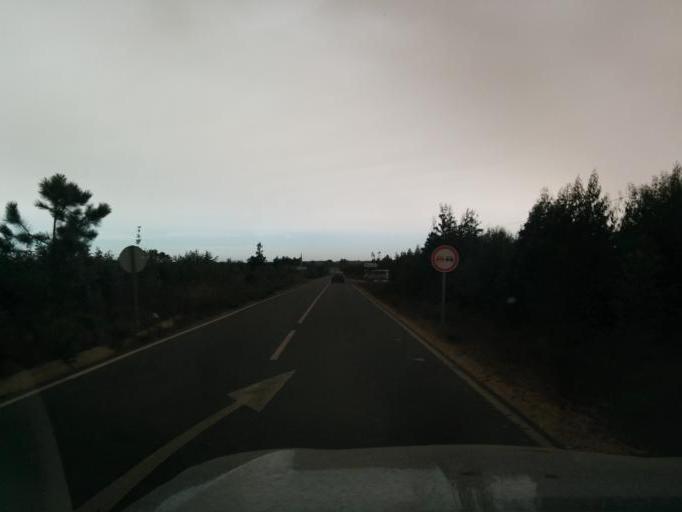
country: PT
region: Beja
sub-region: Odemira
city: Sao Teotonio
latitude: 37.5718
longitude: -8.7372
